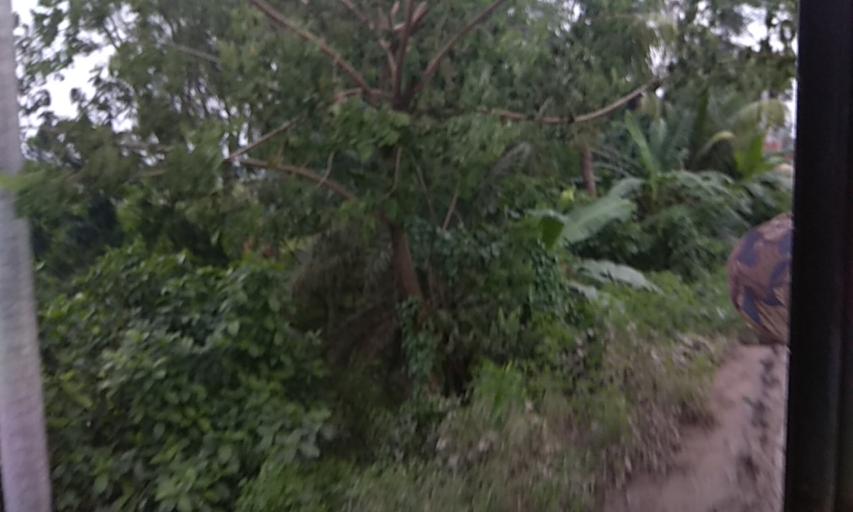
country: BD
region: Dhaka
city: Char Bhadrasan
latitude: 23.3864
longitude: 89.9927
